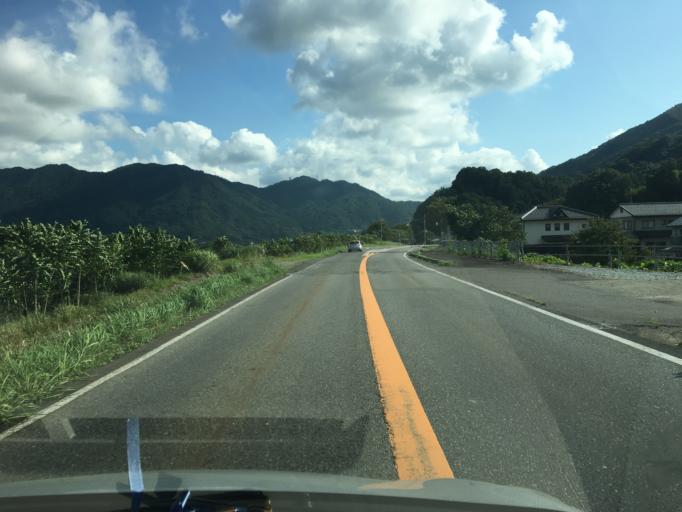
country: JP
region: Hyogo
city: Toyooka
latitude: 35.4361
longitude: 134.7890
